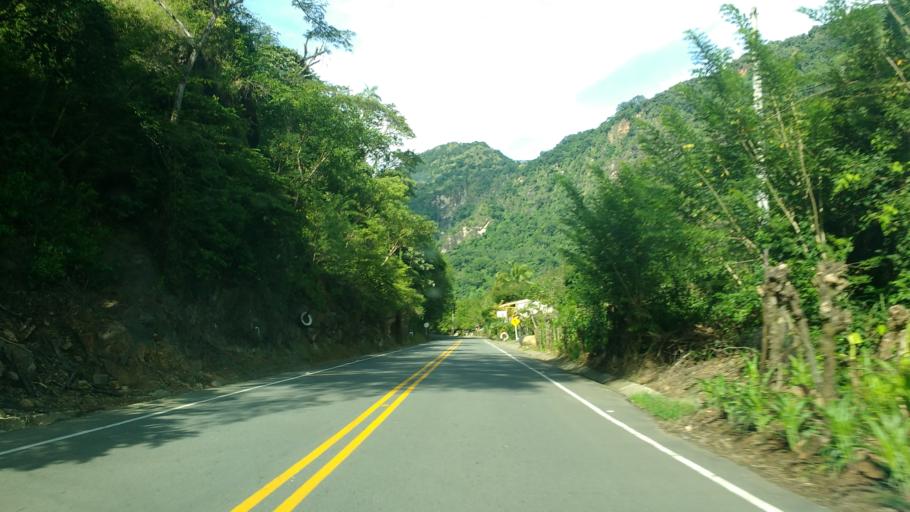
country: CO
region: Antioquia
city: Concordia
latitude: 6.0631
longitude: -75.8633
